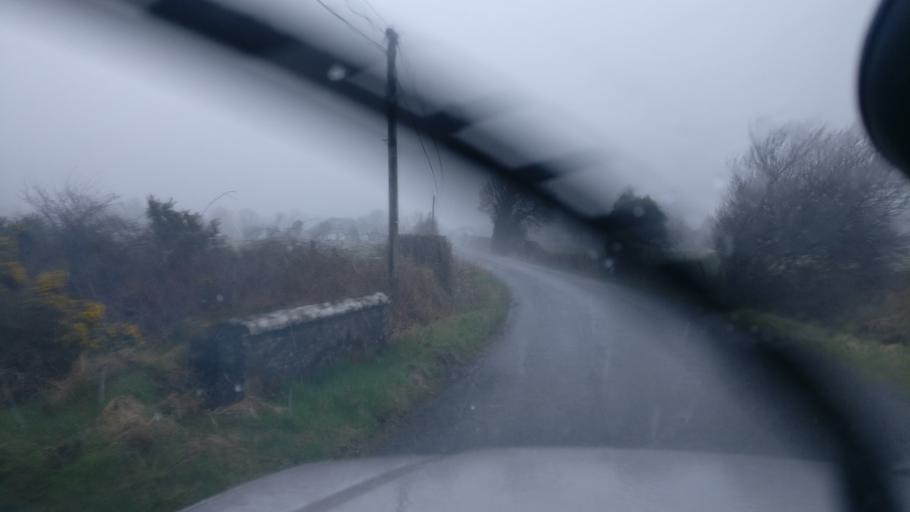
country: IE
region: Connaught
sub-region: County Galway
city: Loughrea
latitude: 53.2275
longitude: -8.3933
